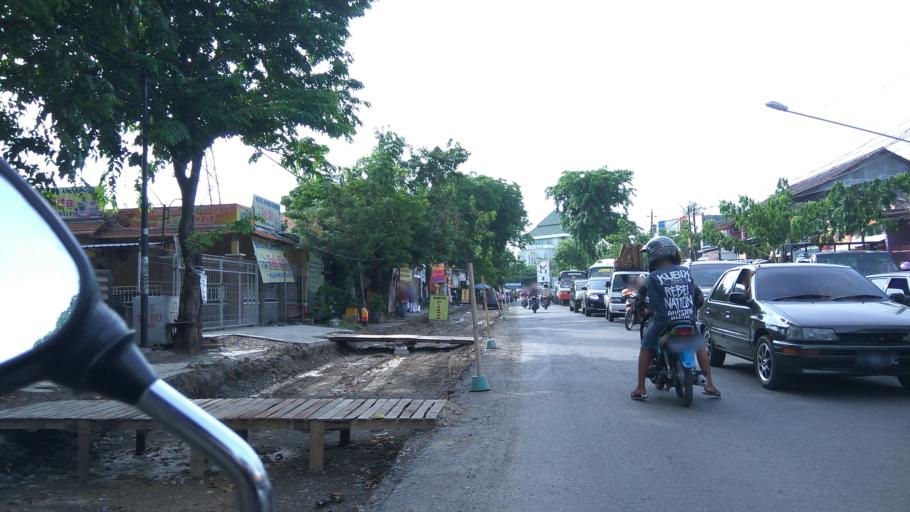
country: ID
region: Central Java
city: Mranggen
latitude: -7.0234
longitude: 110.4643
